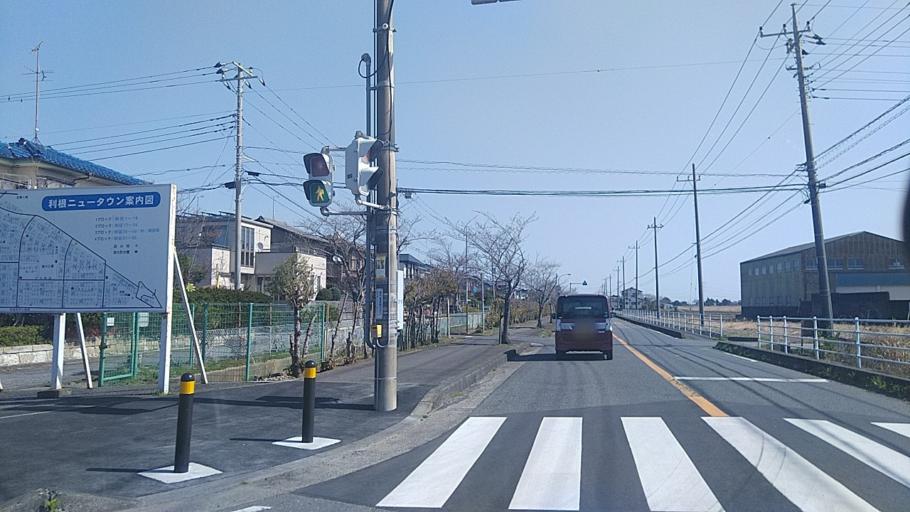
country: JP
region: Ibaraki
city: Ryugasaki
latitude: 35.8561
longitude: 140.1521
